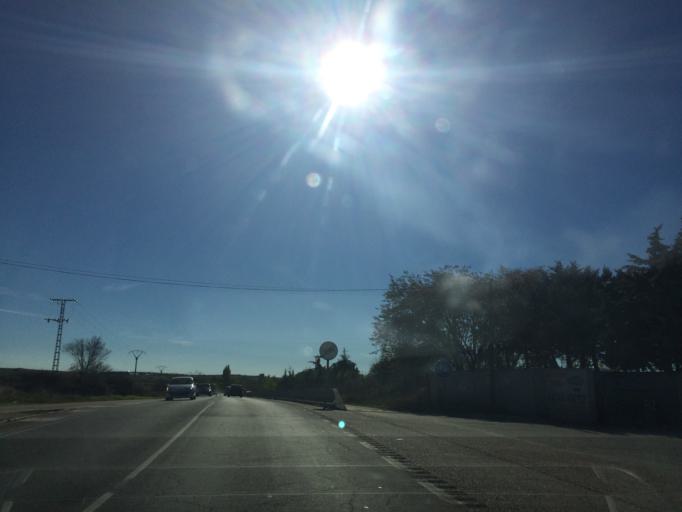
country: ES
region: Madrid
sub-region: Provincia de Madrid
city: Manzanares el Real
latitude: 40.7299
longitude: -3.7901
